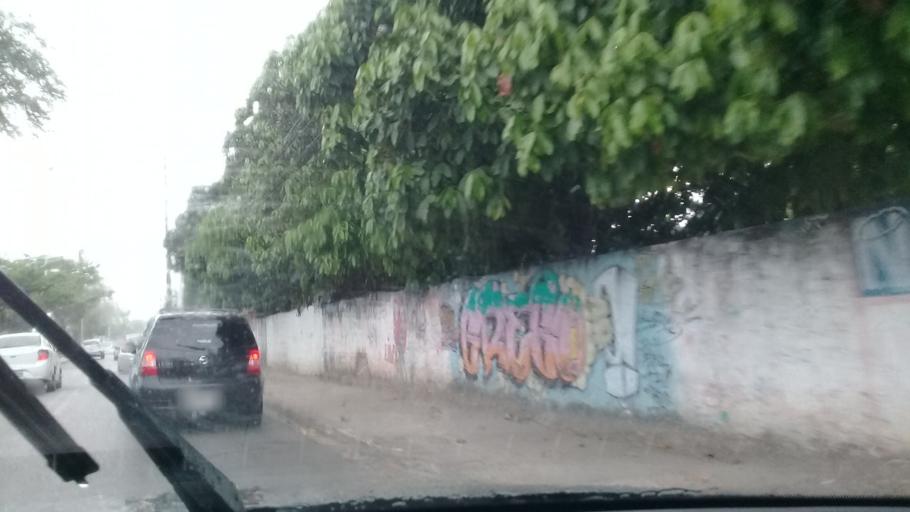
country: BR
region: Pernambuco
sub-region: Recife
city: Recife
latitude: -8.1269
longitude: -34.9101
